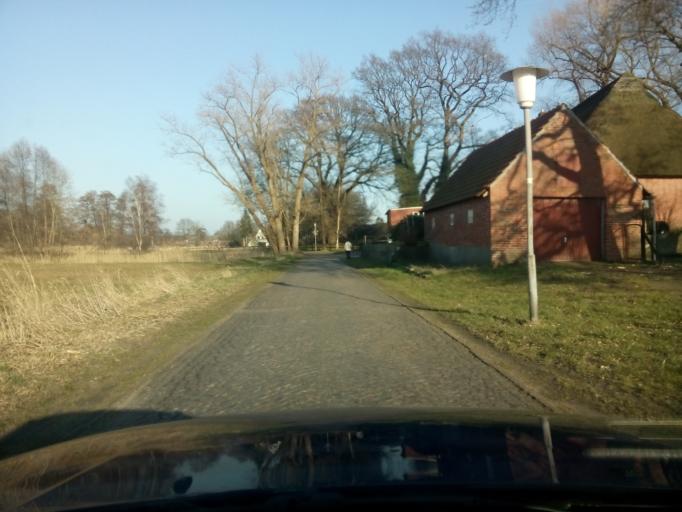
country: DE
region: Lower Saxony
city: Lilienthal
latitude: 53.1346
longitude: 8.8891
